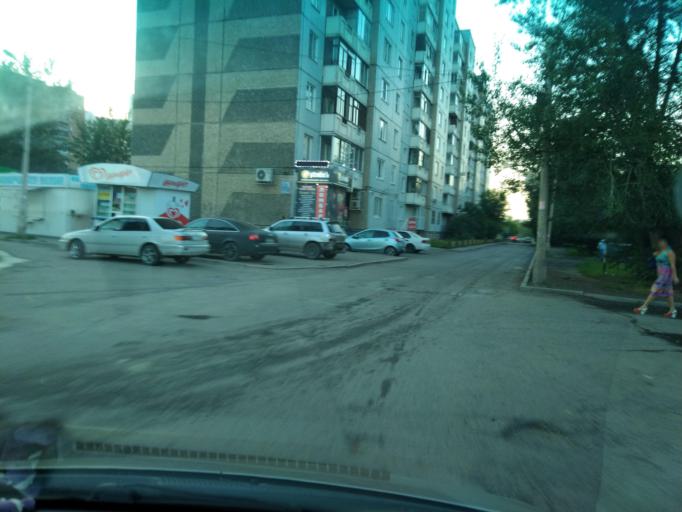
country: RU
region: Krasnoyarskiy
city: Krasnoyarsk
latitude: 55.9860
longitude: 92.8705
